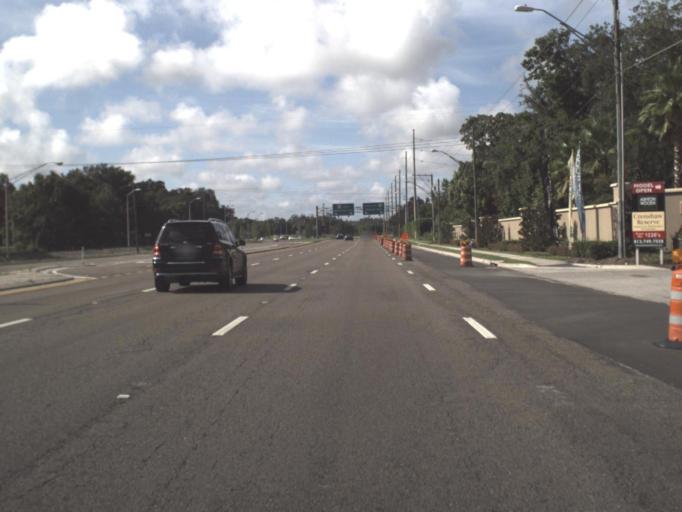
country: US
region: Florida
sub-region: Hillsborough County
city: Lutz
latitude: 28.1143
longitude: -82.4613
